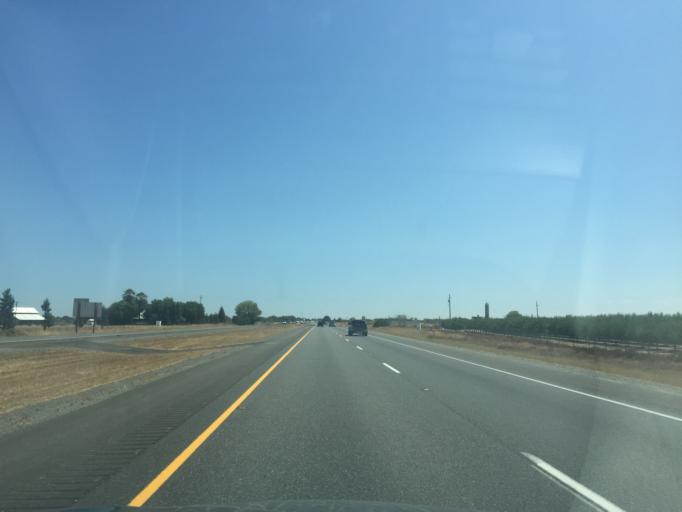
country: US
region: California
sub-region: Tehama County
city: Corning
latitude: 39.9839
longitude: -122.2033
